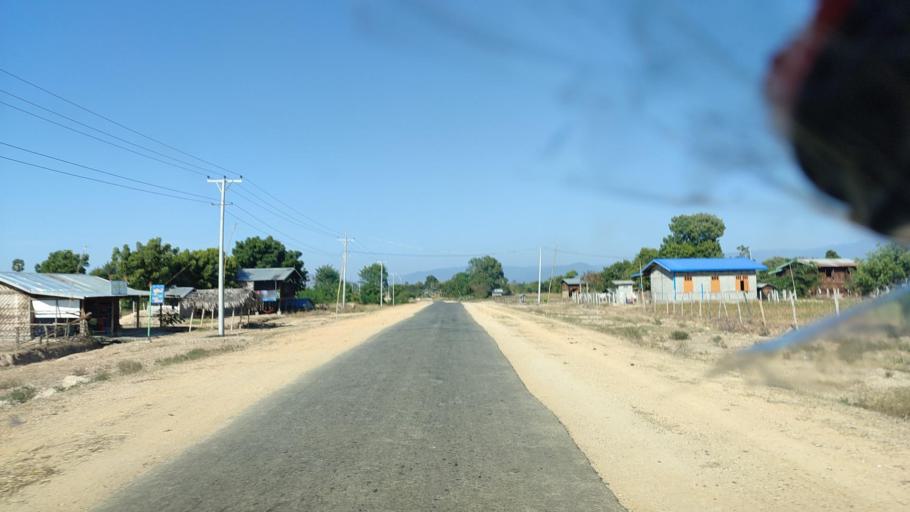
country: MM
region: Mandalay
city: Yamethin
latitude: 20.1712
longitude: 96.2612
